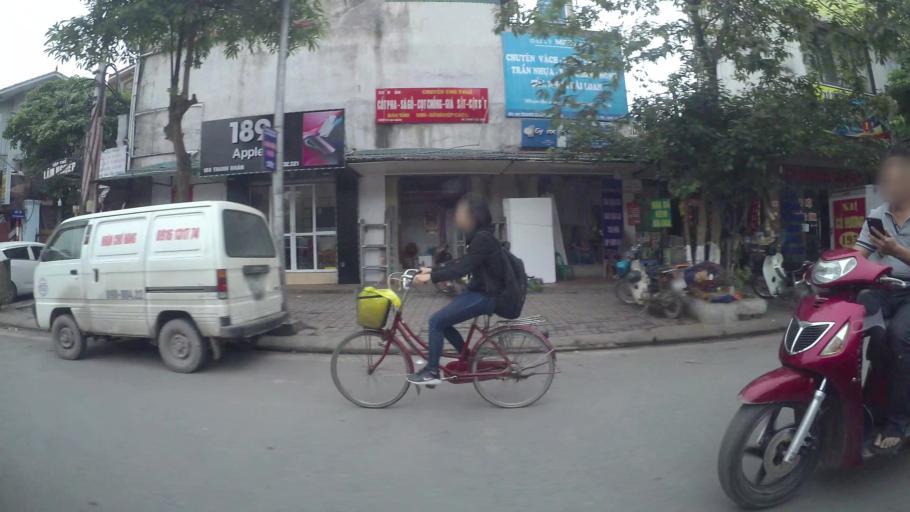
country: VN
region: Ha Noi
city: Hai BaTrung
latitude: 21.0030
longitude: 105.8553
